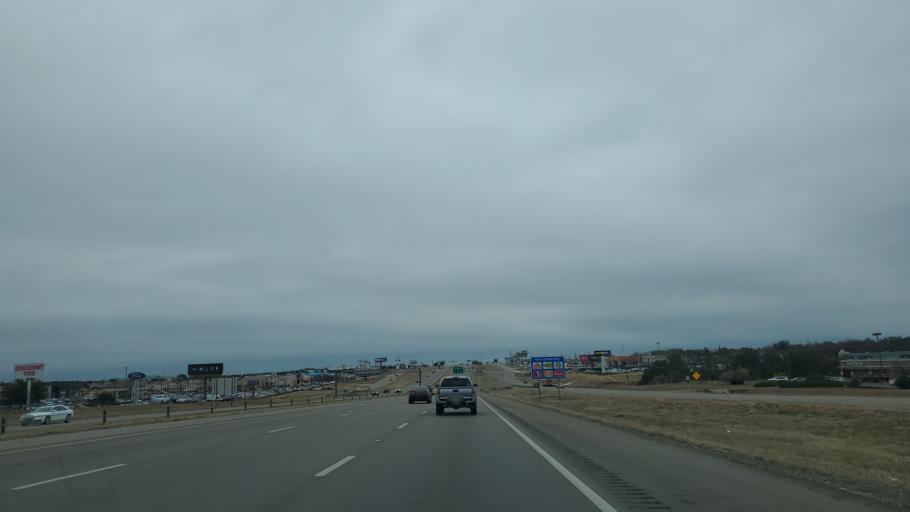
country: US
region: Texas
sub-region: Bell County
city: Killeen
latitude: 31.0859
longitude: -97.7100
